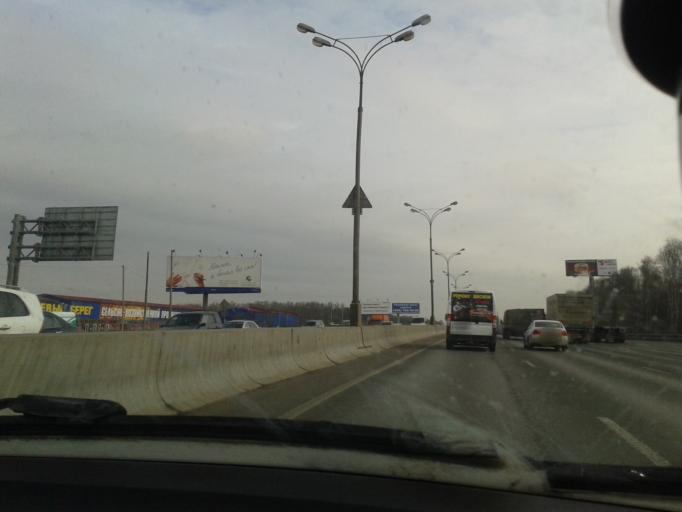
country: RU
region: Moscow
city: Businovo
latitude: 55.8948
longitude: 37.5028
